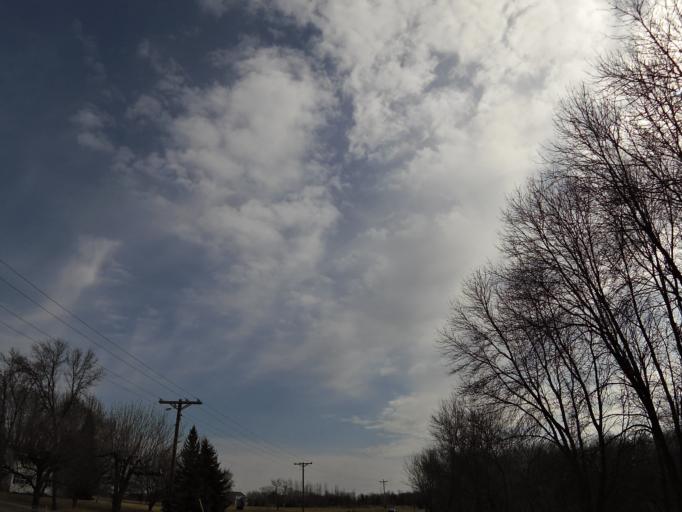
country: US
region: Minnesota
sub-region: Scott County
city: Prior Lake
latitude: 44.6910
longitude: -93.3796
